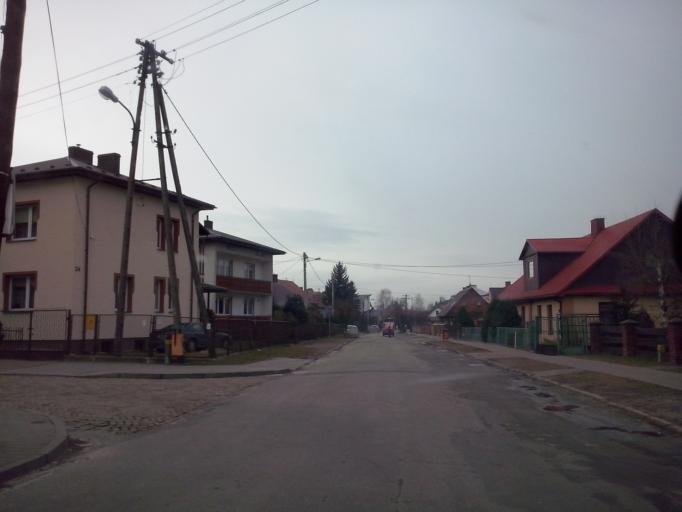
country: PL
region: Lublin Voivodeship
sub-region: Powiat bilgorajski
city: Bilgoraj
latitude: 50.5453
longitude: 22.7244
